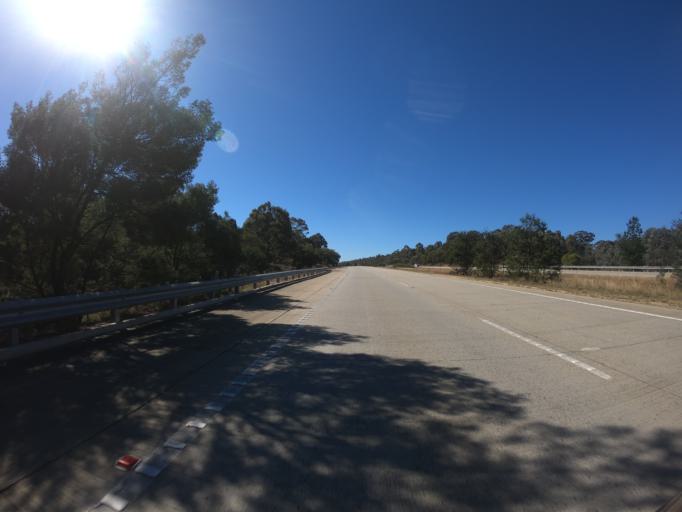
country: AU
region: New South Wales
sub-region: Yass Valley
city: Gundaroo
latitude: -35.1120
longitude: 149.3647
